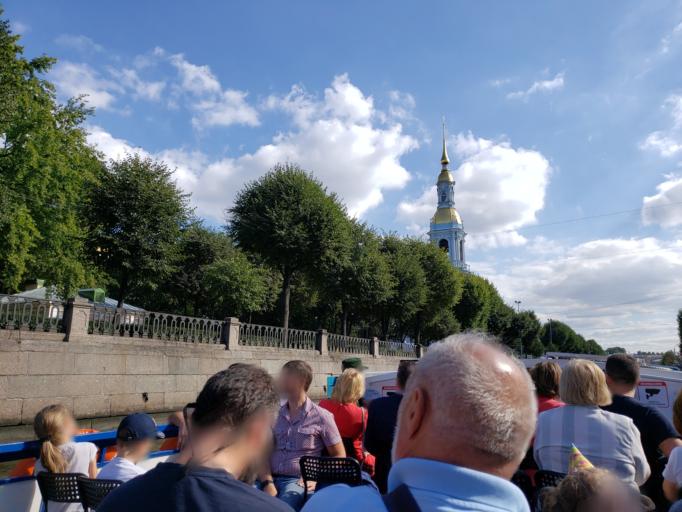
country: RU
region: St.-Petersburg
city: Admiralteisky
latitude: 59.9229
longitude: 30.2971
